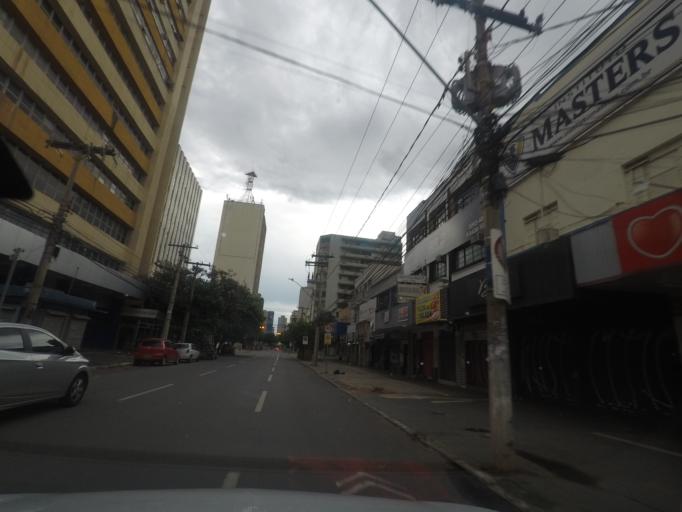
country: BR
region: Goias
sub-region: Goiania
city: Goiania
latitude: -16.6761
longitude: -49.2587
